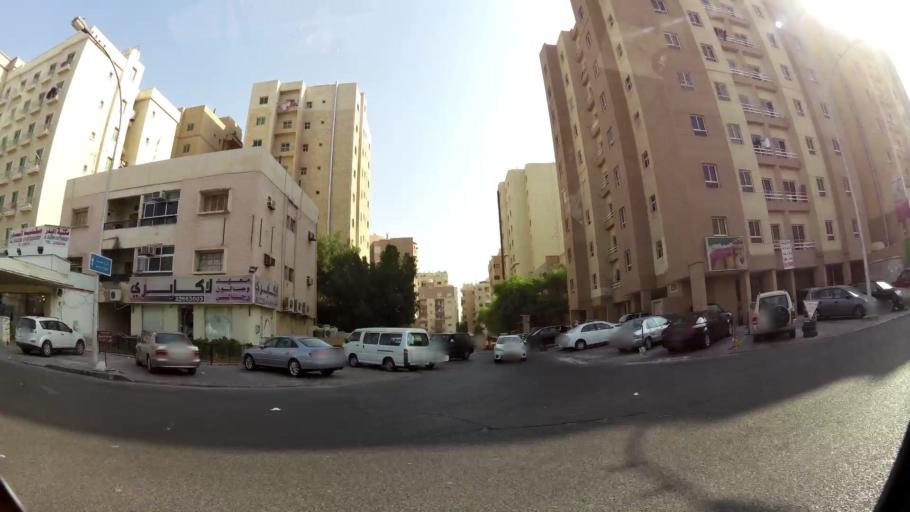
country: KW
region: Muhafazat Hawalli
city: Hawalli
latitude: 29.3359
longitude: 48.0072
